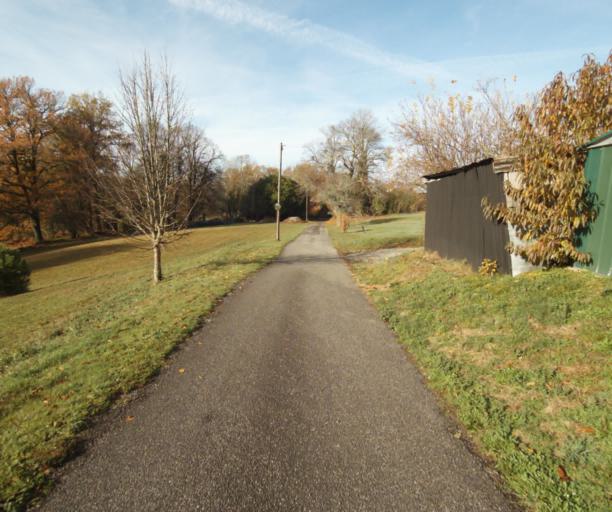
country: FR
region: Limousin
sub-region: Departement de la Correze
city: Sainte-Fortunade
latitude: 45.2196
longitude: 1.7476
